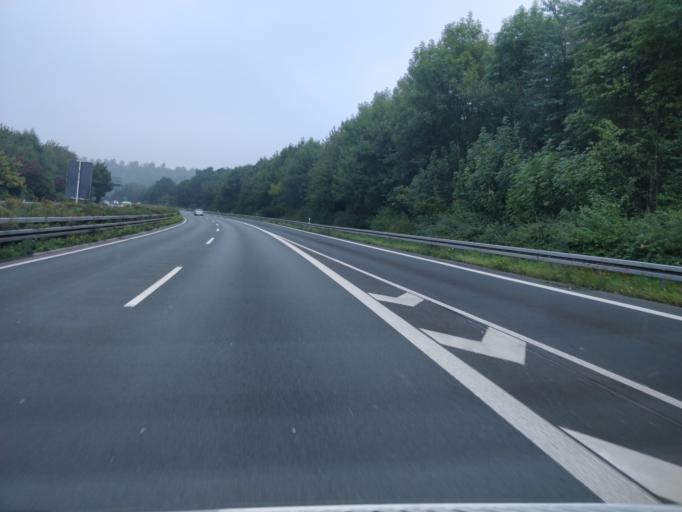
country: DE
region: North Rhine-Westphalia
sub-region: Regierungsbezirk Dusseldorf
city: Dinslaken
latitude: 51.5299
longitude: 6.7585
